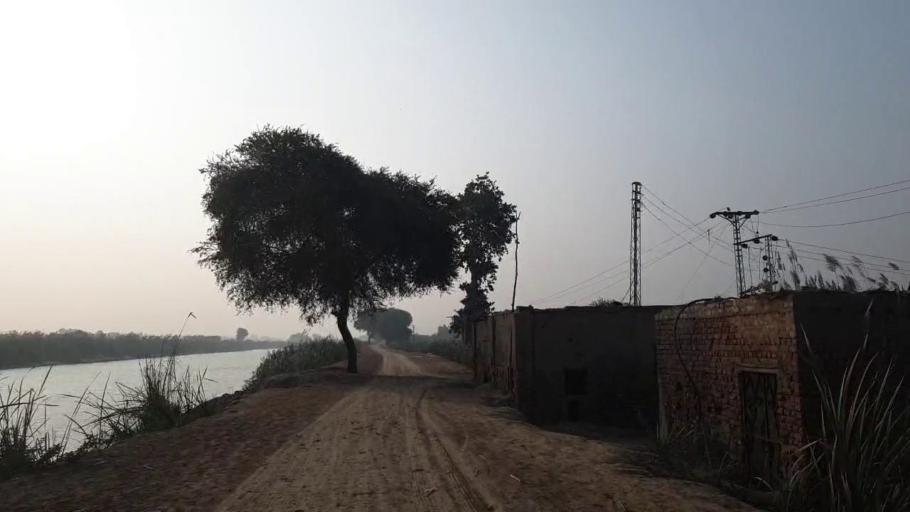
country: PK
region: Sindh
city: Tando Muhammad Khan
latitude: 25.1146
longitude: 68.5679
